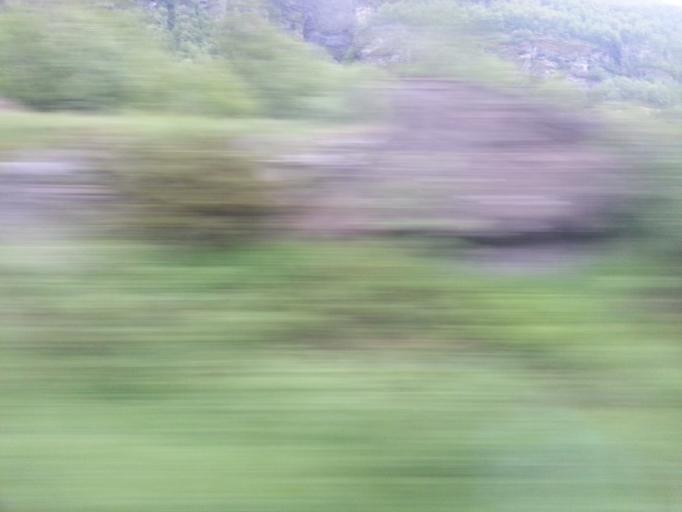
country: NO
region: Sor-Trondelag
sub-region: Oppdal
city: Oppdal
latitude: 62.4623
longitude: 9.5753
